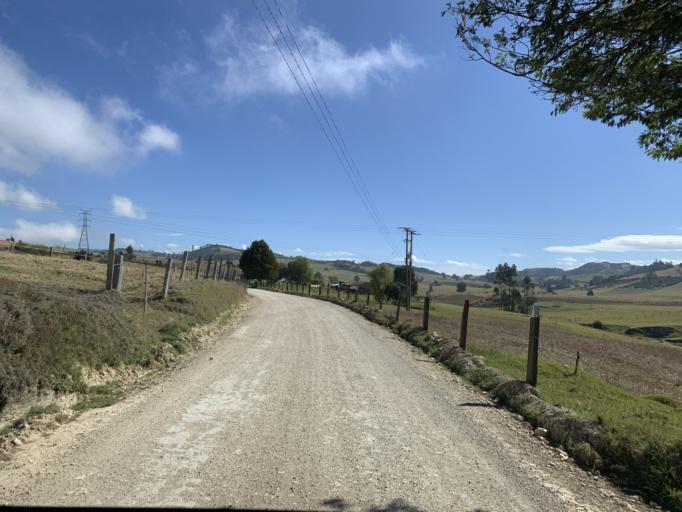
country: CO
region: Boyaca
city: Tuta
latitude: 5.6713
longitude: -73.1488
